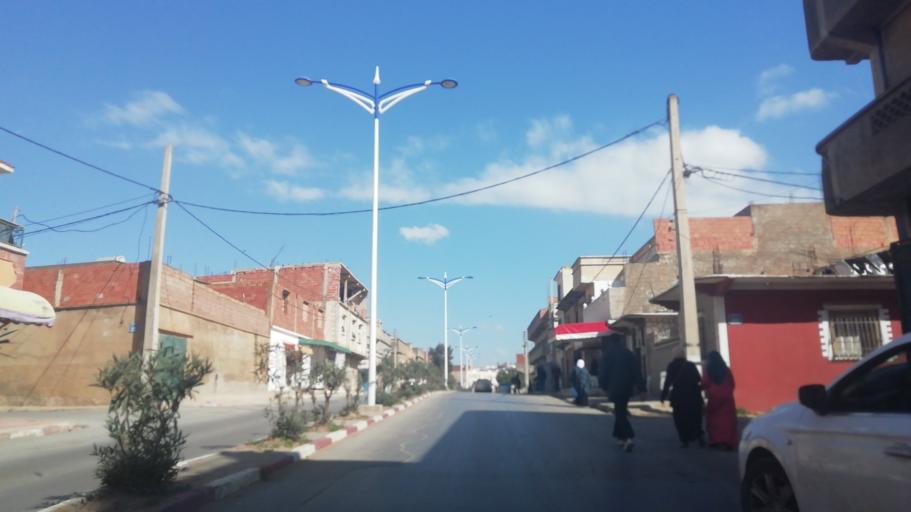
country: DZ
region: Mostaganem
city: Mostaganem
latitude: 35.9956
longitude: 0.3019
